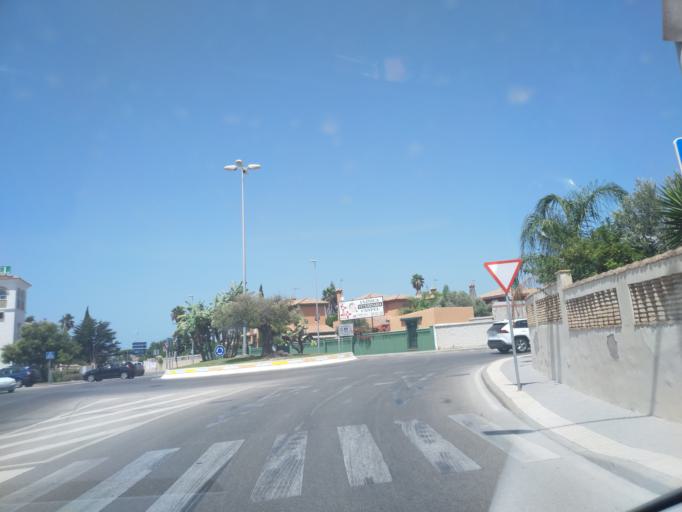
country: ES
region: Andalusia
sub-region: Provincia de Cadiz
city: Chiclana de la Frontera
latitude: 36.3962
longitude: -6.1723
